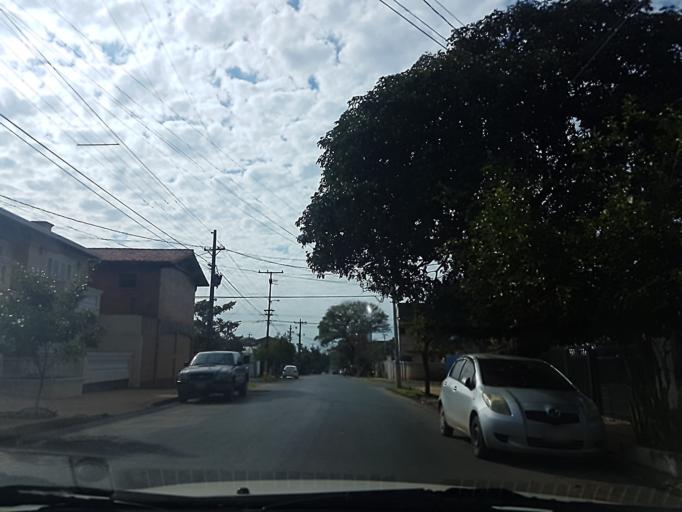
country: PY
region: Asuncion
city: Asuncion
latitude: -25.2669
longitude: -57.5660
